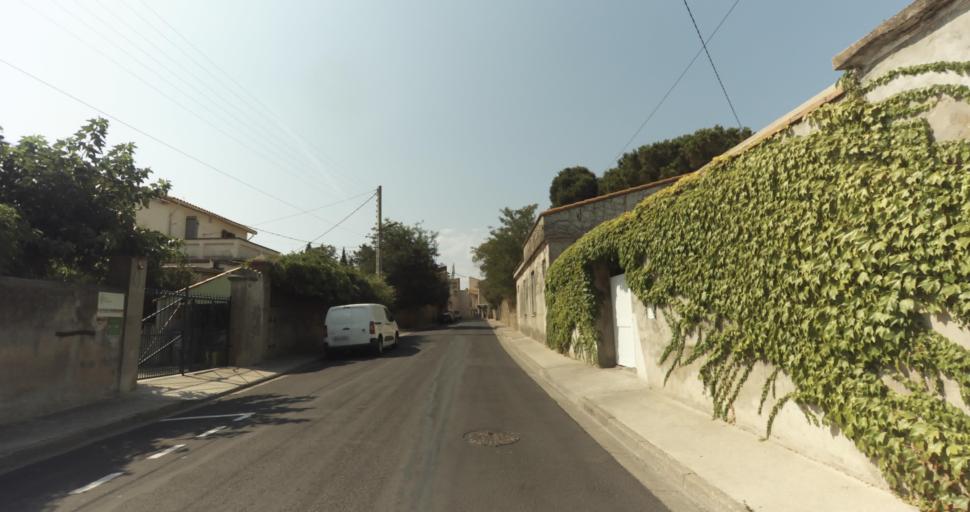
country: FR
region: Languedoc-Roussillon
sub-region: Departement des Pyrenees-Orientales
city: Latour-Bas-Elne
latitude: 42.6072
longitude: 3.0015
